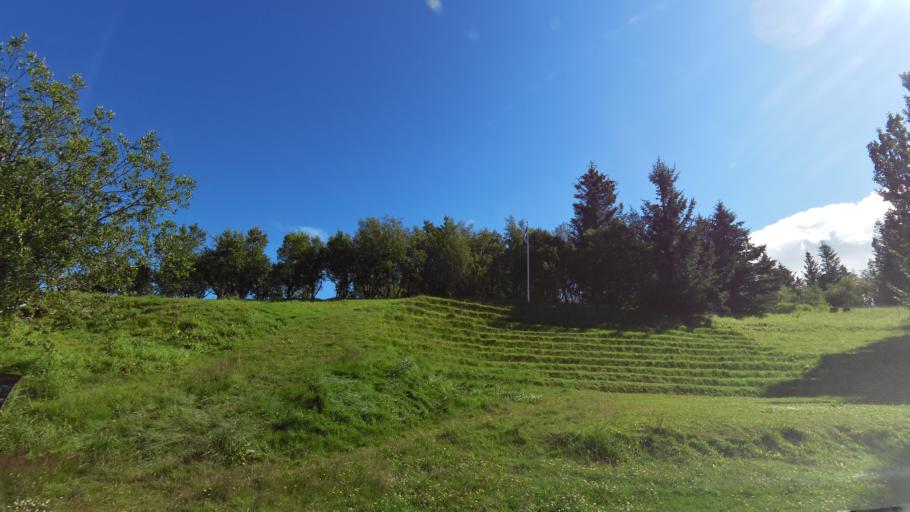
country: IS
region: Capital Region
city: Mosfellsbaer
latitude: 64.1665
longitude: -21.6781
